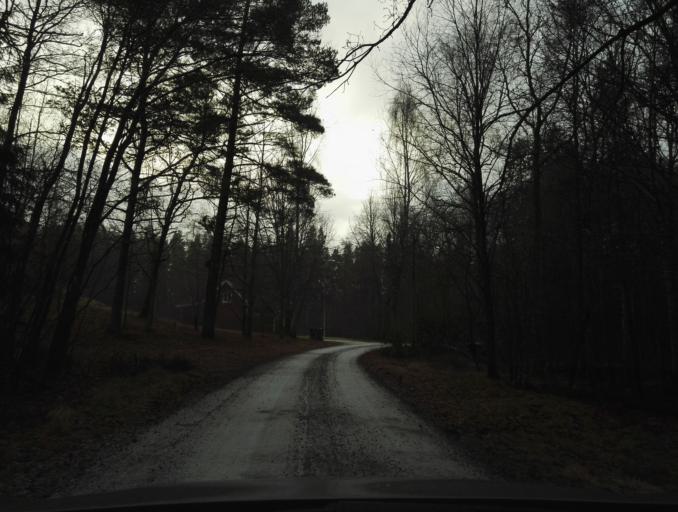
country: SE
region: Kronoberg
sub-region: Vaxjo Kommun
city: Vaexjoe
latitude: 56.9217
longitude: 14.7508
